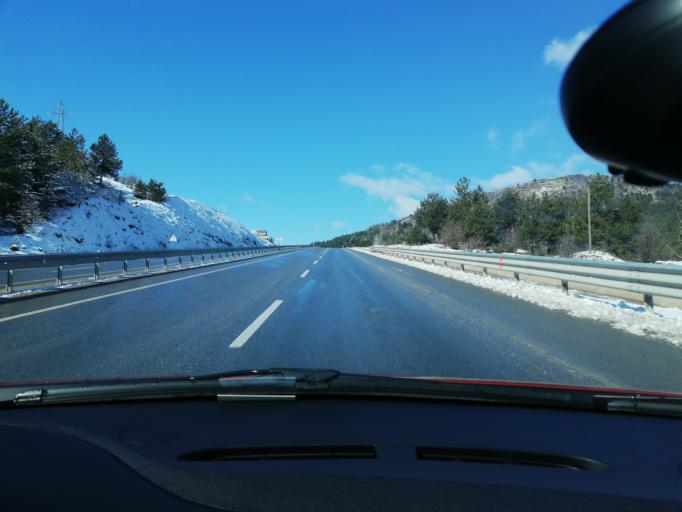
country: TR
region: Kastamonu
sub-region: Cide
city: Kastamonu
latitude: 41.3602
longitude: 33.7014
